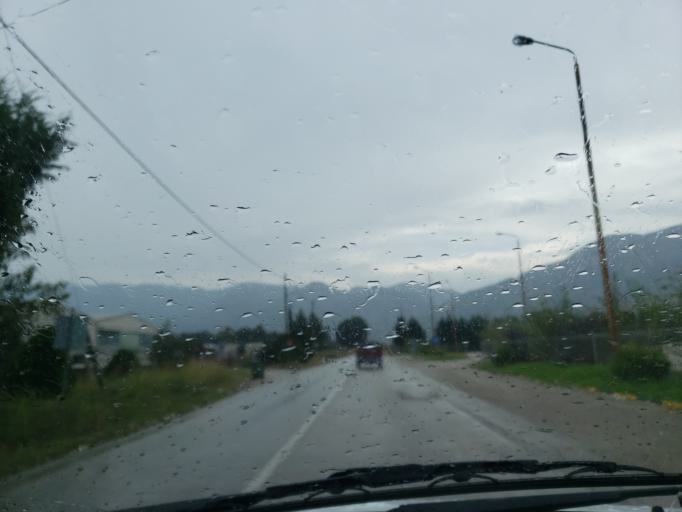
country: GR
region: Central Greece
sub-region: Nomos Fthiotidos
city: Anthili
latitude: 38.8206
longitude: 22.4419
